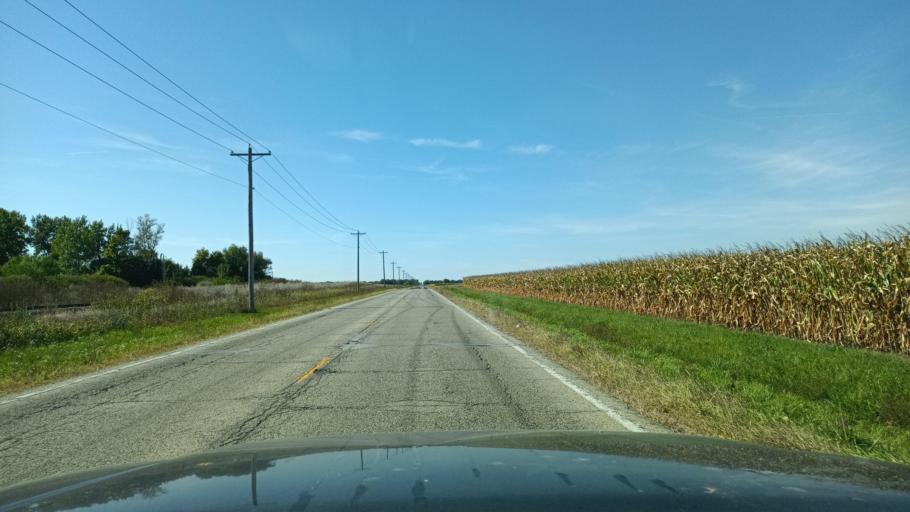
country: US
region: Illinois
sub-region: Champaign County
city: Mahomet
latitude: 40.2040
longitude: -88.4648
